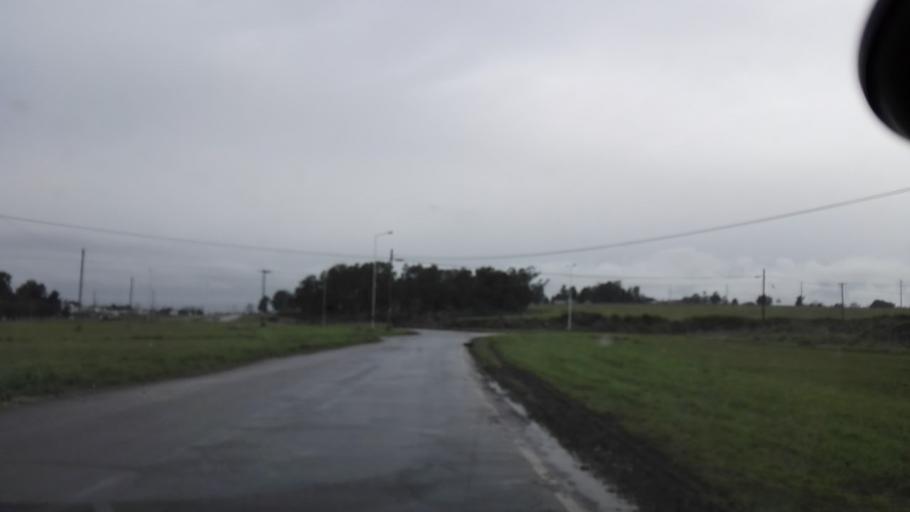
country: AR
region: Buenos Aires
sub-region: Partido de Tandil
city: Tandil
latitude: -37.2981
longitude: -59.1841
